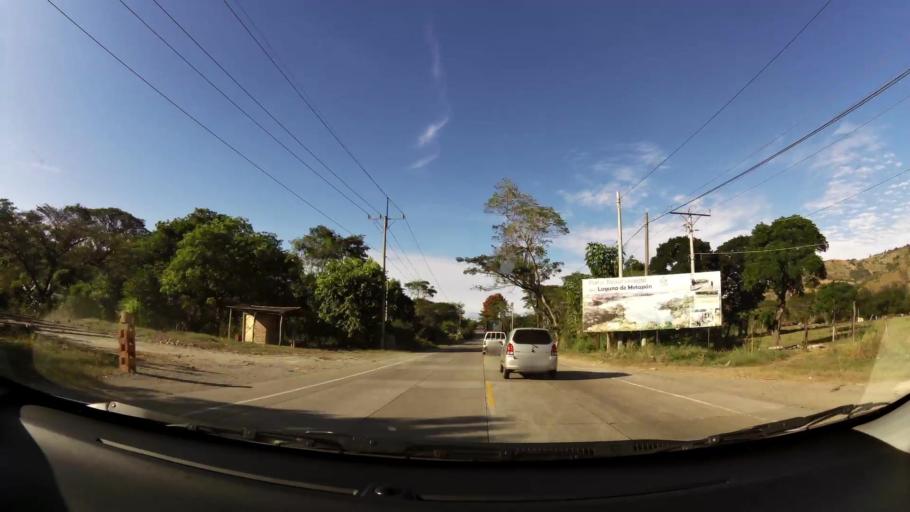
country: SV
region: Santa Ana
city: Metapan
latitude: 14.2836
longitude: -89.4617
